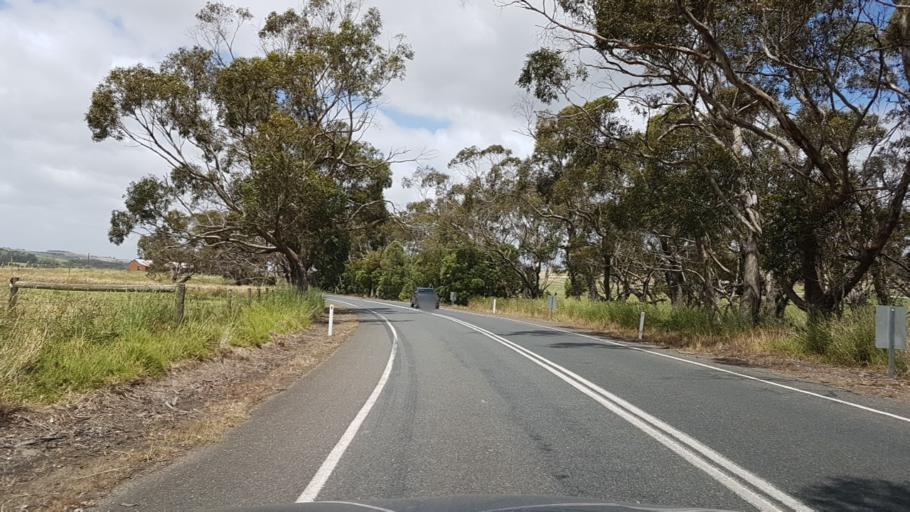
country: AU
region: South Australia
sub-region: Alexandrina
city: Mount Compass
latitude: -35.4174
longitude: 138.5515
